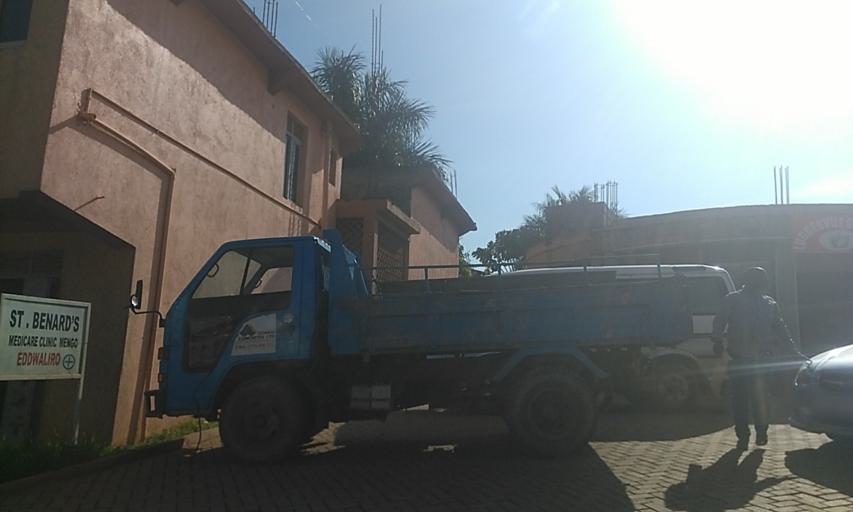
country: UG
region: Central Region
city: Kampala Central Division
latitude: 0.3242
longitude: 32.5407
